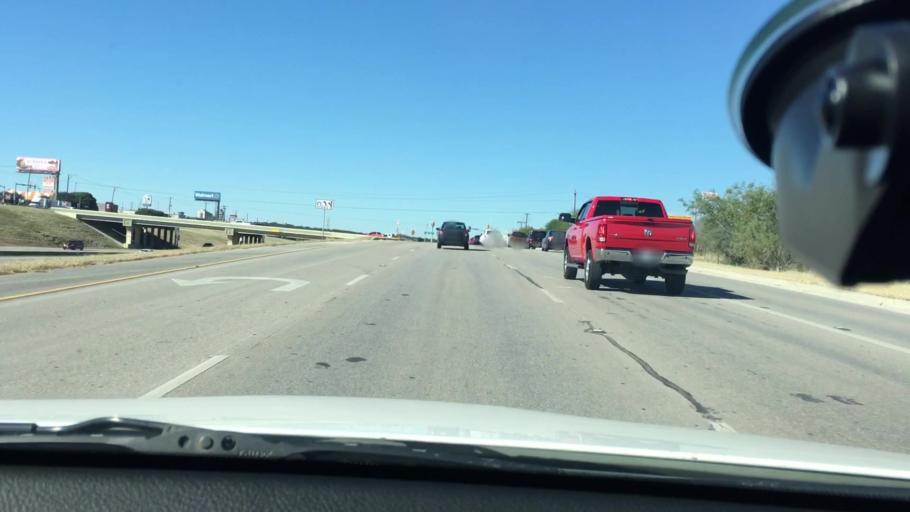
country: US
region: Texas
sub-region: Bexar County
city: Live Oak
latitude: 29.5902
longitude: -98.3502
